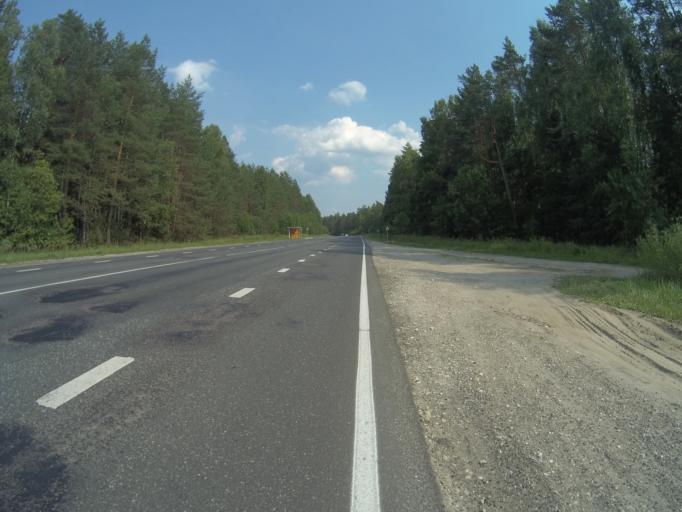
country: RU
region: Vladimir
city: Muromtsevo
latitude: 55.9537
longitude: 41.0039
